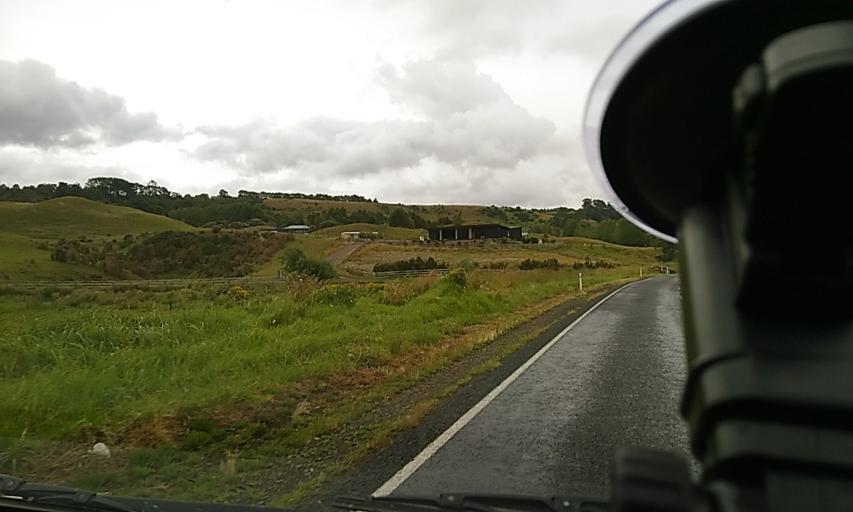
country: NZ
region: Auckland
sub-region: Auckland
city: Pukekohe East
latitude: -37.3146
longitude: 174.9532
